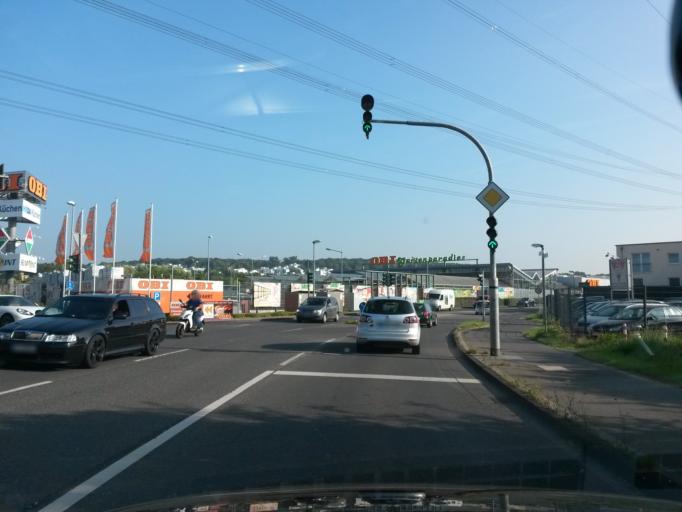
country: DE
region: North Rhine-Westphalia
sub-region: Regierungsbezirk Koln
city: Alfter
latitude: 50.7186
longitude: 7.0298
